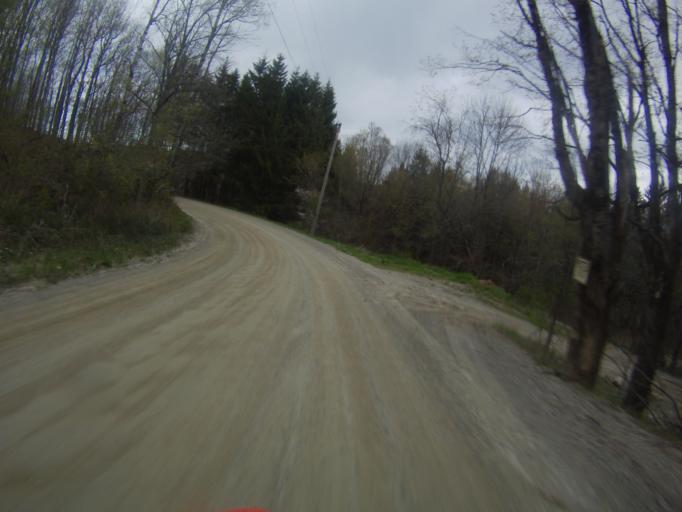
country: US
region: Vermont
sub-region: Addison County
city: Bristol
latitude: 44.0569
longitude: -73.0197
